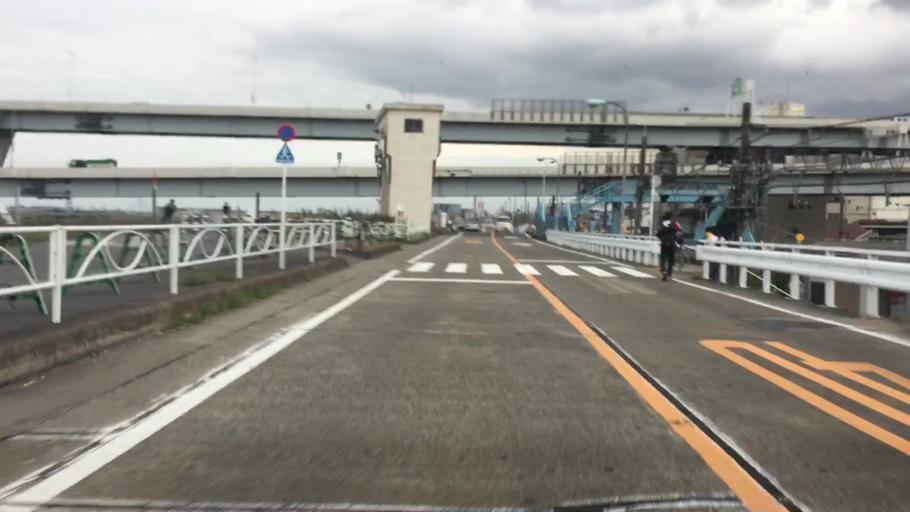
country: JP
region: Saitama
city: Soka
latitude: 35.7435
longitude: 139.8177
